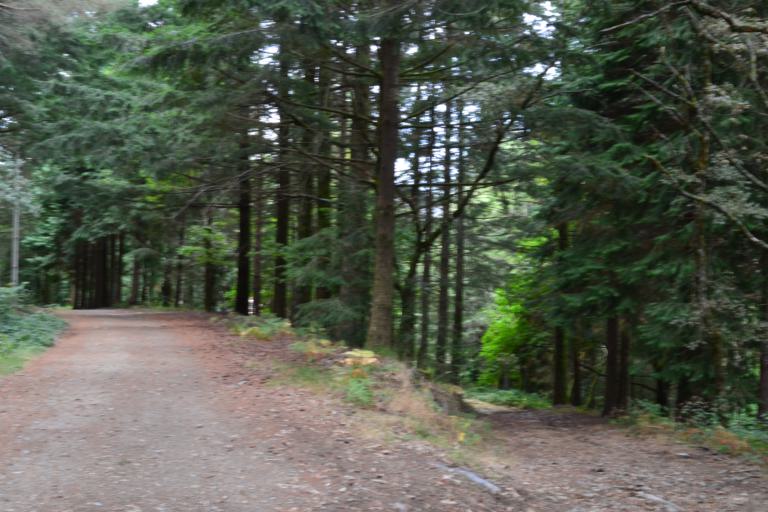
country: PT
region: Vila Real
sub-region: Santa Marta de Penaguiao
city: Santa Marta de Penaguiao
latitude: 41.2756
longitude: -7.8925
